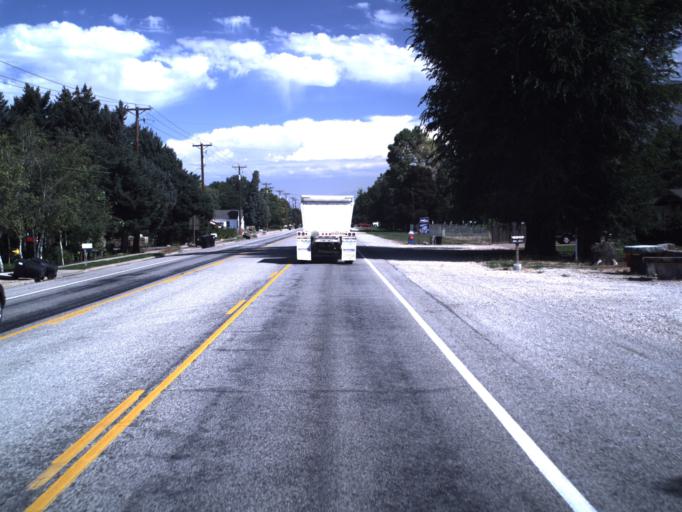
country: US
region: Utah
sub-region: Weber County
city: Farr West
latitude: 41.2981
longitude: -112.0277
